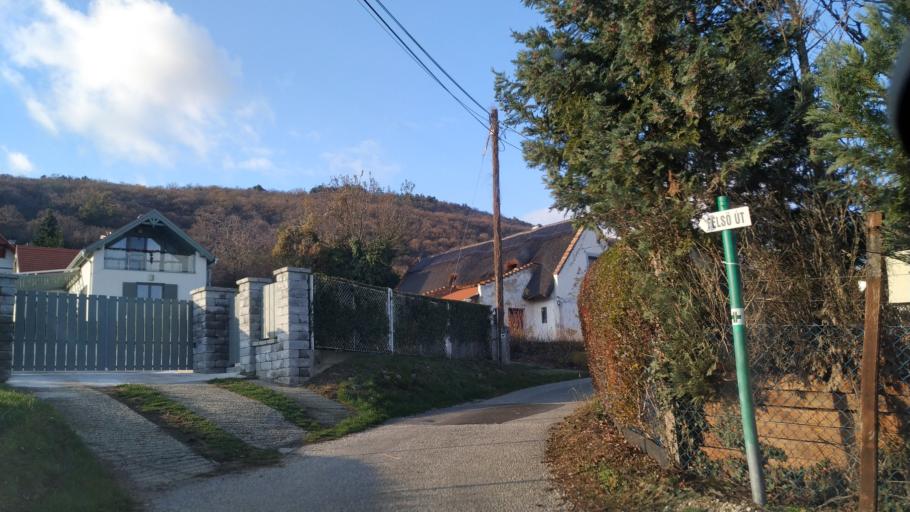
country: HU
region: Zala
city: Vonyarcvashegy
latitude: 46.7807
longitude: 17.3636
